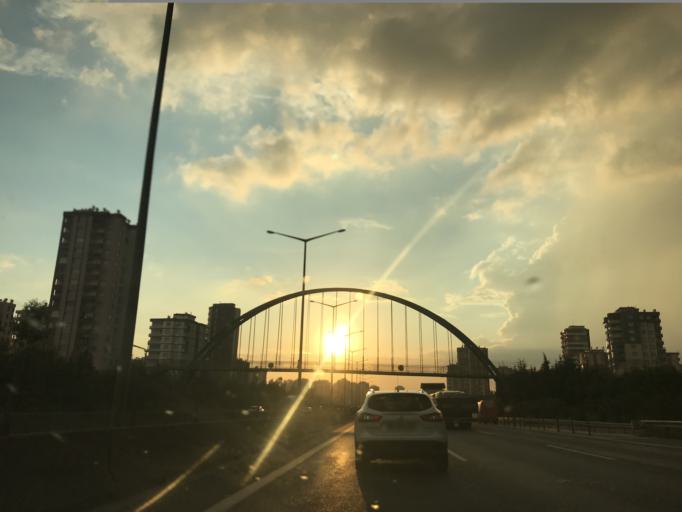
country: TR
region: Adana
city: Seyhan
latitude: 37.0319
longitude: 35.2873
